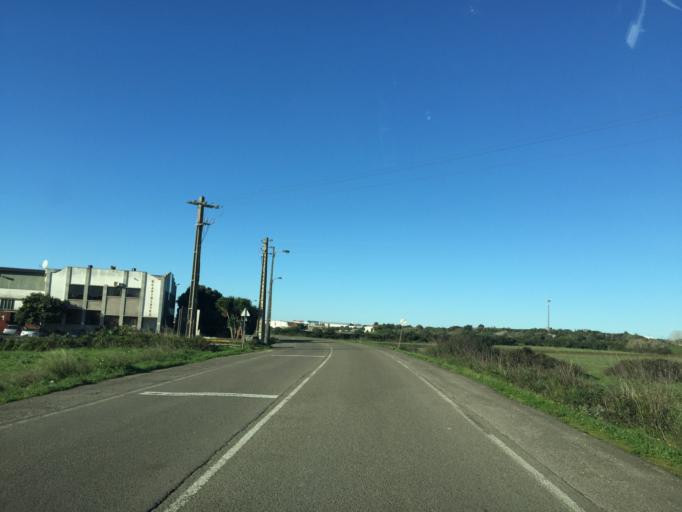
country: PT
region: Lisbon
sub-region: Sintra
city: Pero Pinheiro
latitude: 38.8607
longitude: -9.3126
